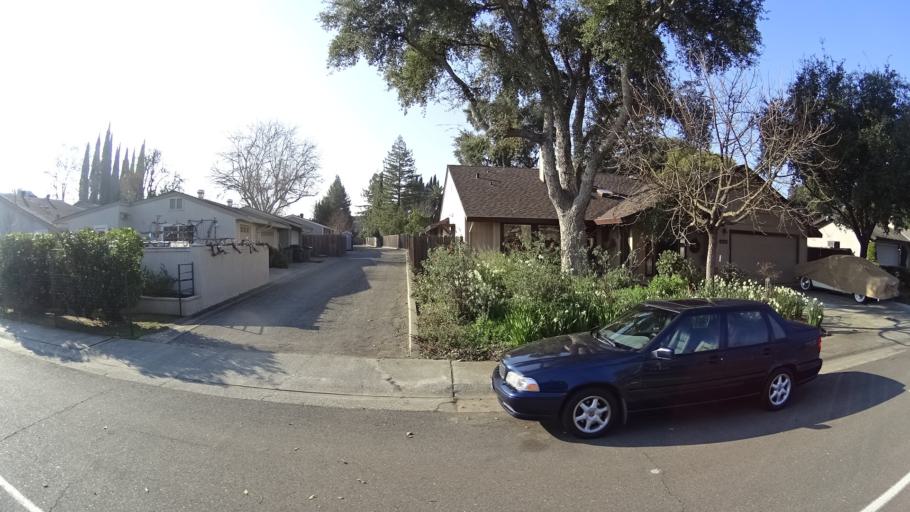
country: US
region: California
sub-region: Yolo County
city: Davis
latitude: 38.5555
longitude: -121.7884
